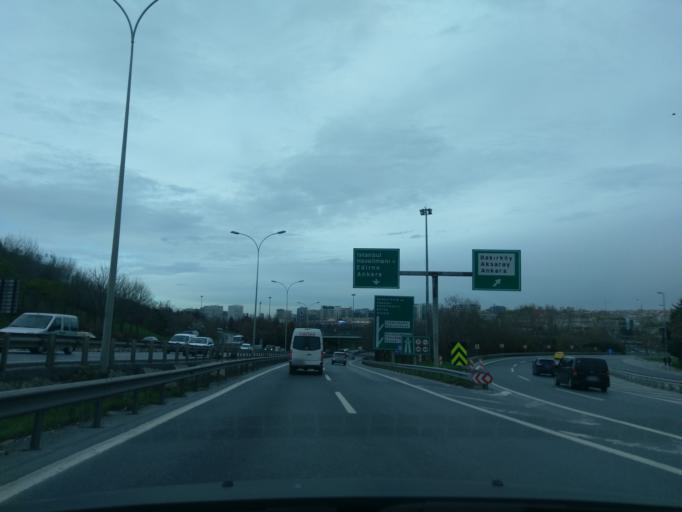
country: TR
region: Istanbul
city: Bahcelievler
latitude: 40.9899
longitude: 28.8185
